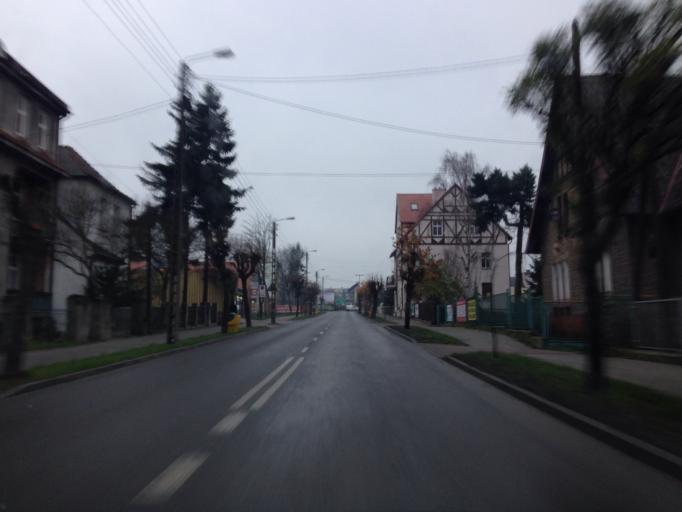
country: PL
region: Kujawsko-Pomorskie
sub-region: Powiat nakielski
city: Naklo nad Notecia
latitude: 53.1398
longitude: 17.6042
